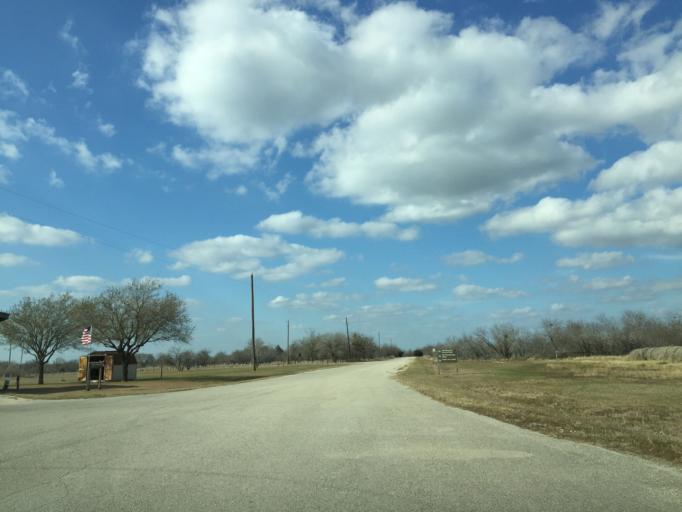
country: US
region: Texas
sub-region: Williamson County
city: Granger
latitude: 30.6661
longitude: -97.3651
